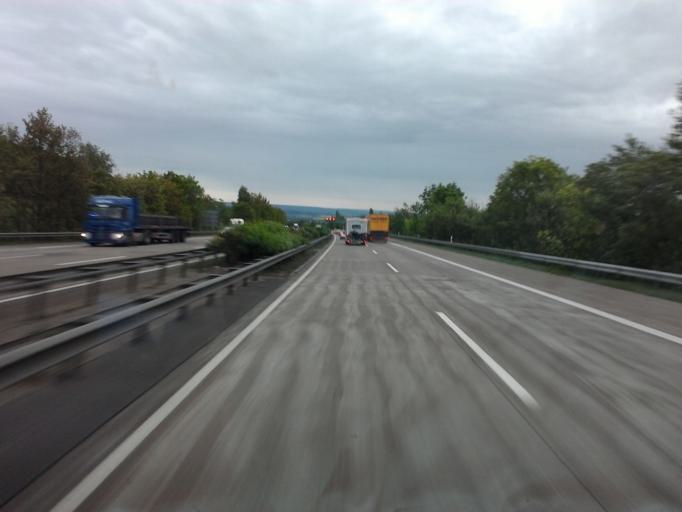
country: DE
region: Rheinland-Pfalz
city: Bell
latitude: 50.3947
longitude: 7.2465
